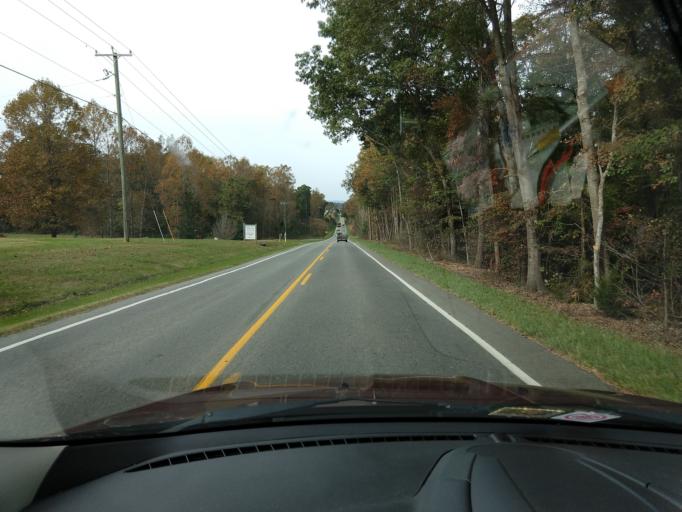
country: US
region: Virginia
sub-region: Franklin County
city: Union Hall
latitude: 36.9847
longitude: -79.6382
